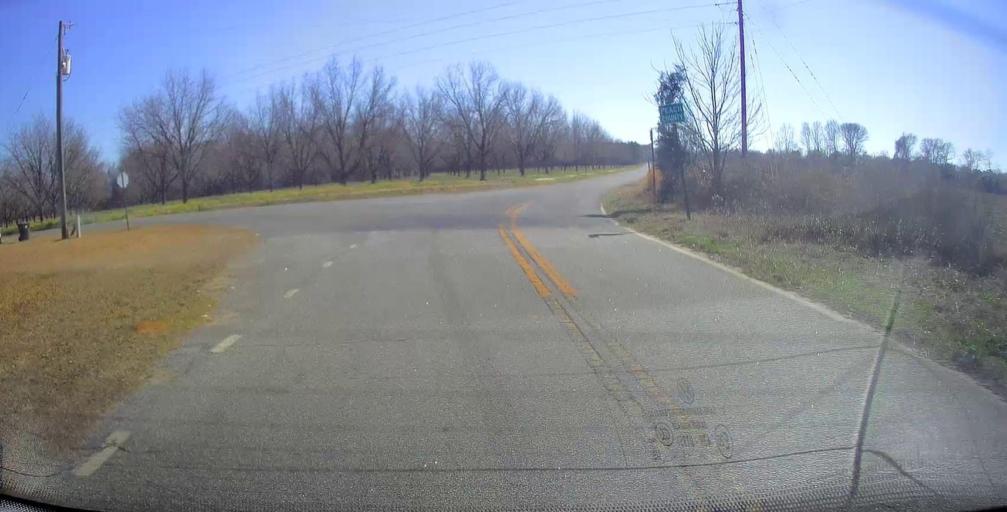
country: US
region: Georgia
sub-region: Peach County
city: Fort Valley
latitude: 32.6329
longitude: -83.8543
